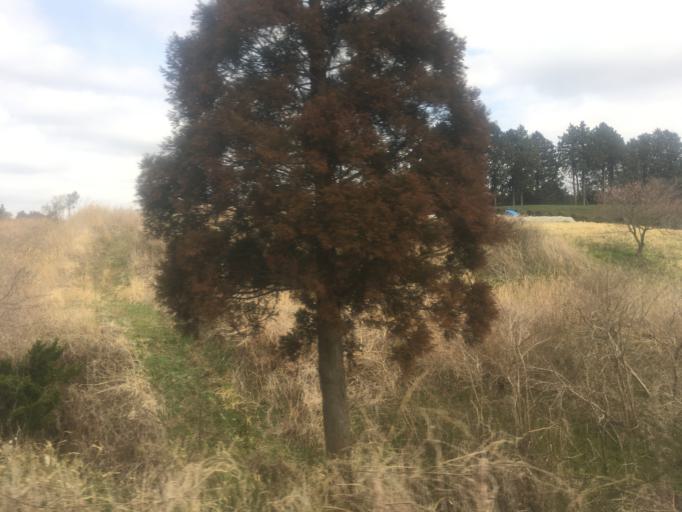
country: JP
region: Chiba
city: Yachimata
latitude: 35.6557
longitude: 140.3305
